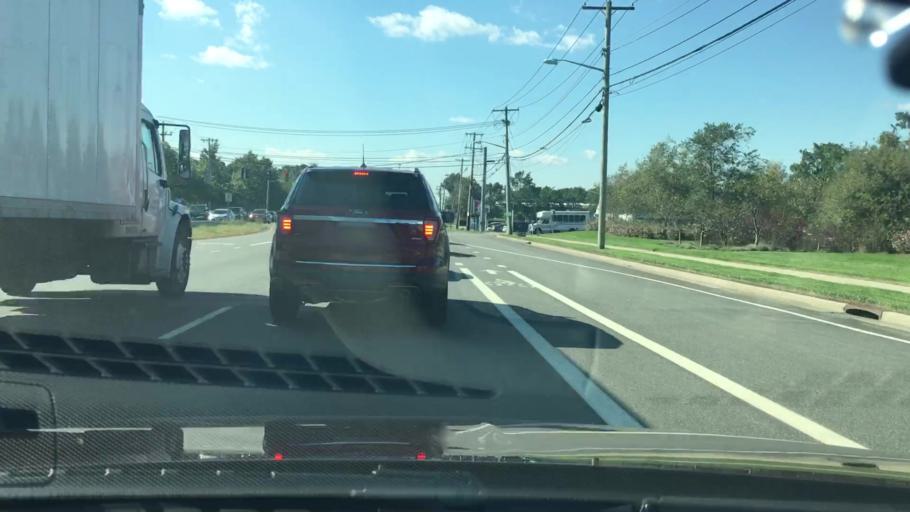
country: US
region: New York
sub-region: Suffolk County
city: Bohemia
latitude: 40.7871
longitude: -73.1233
